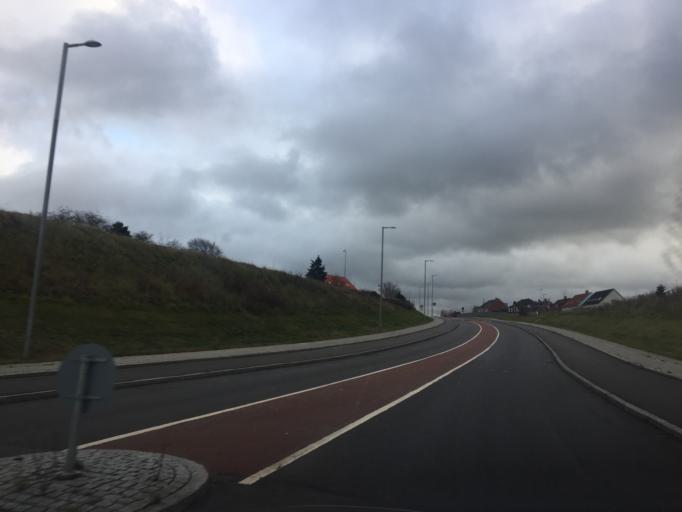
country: DK
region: Zealand
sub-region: Holbaek Kommune
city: Tollose
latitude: 55.6147
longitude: 11.7703
